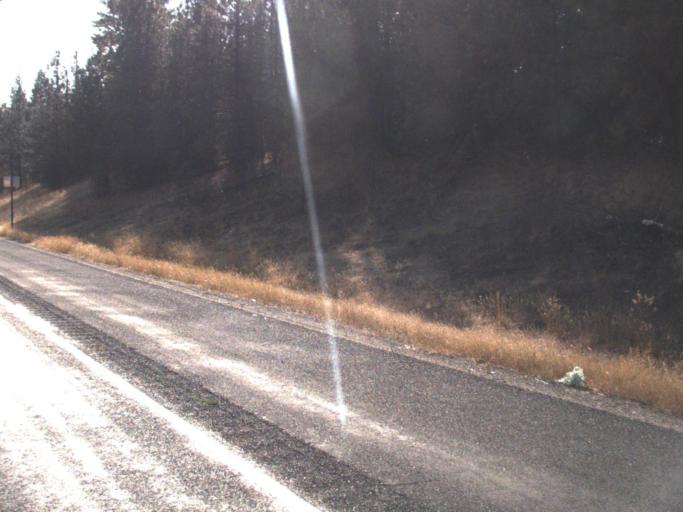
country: US
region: Washington
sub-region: Spokane County
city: Deer Park
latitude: 48.0680
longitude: -117.3373
